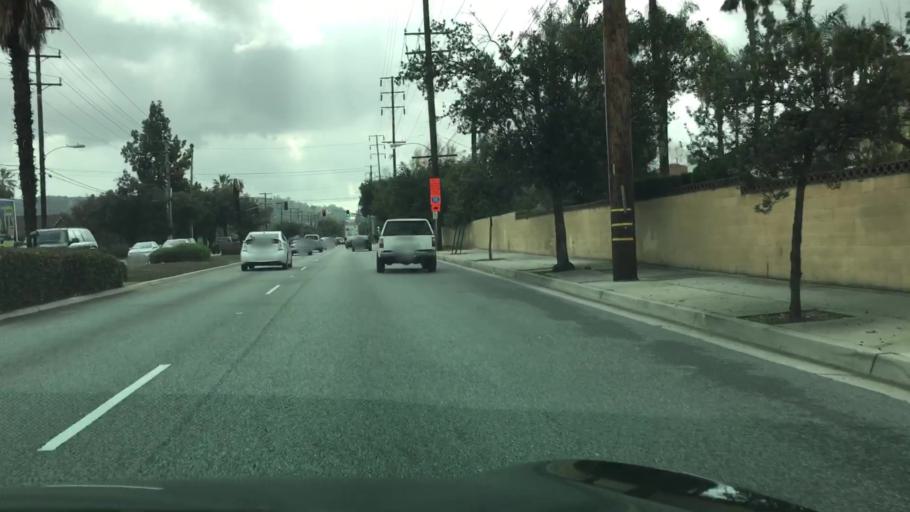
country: US
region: California
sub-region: Los Angeles County
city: West Covina
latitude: 34.0625
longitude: -117.9079
